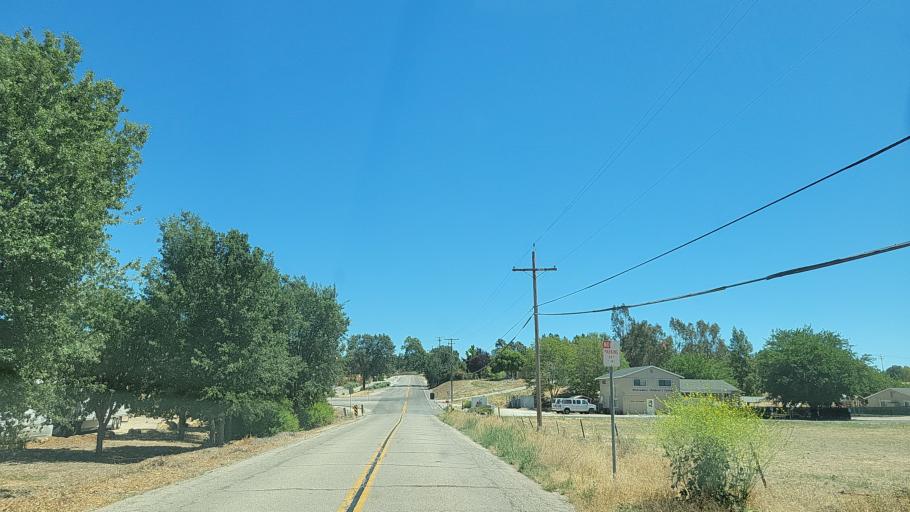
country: US
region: California
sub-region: San Luis Obispo County
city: Atascadero
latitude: 35.4519
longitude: -120.6343
